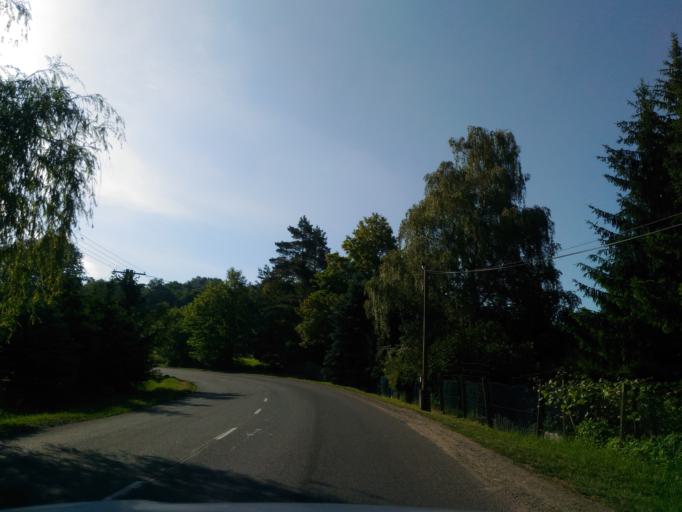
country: HU
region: Baranya
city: Komlo
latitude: 46.1859
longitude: 18.3015
